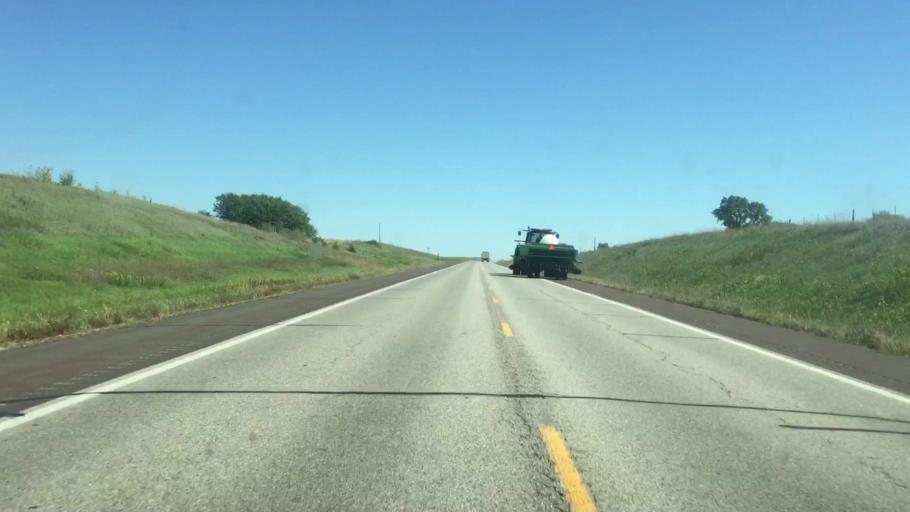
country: US
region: Kansas
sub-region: Nemaha County
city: Seneca
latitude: 39.8421
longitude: -96.2815
